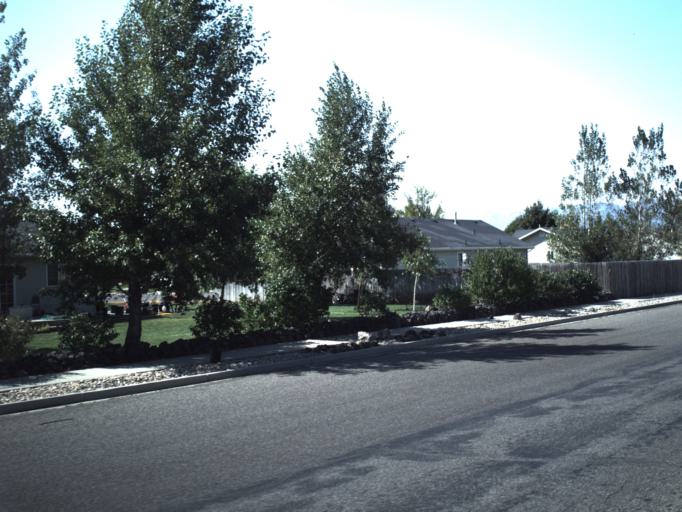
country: US
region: Utah
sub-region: Cache County
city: Hyrum
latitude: 41.6344
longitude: -111.8172
